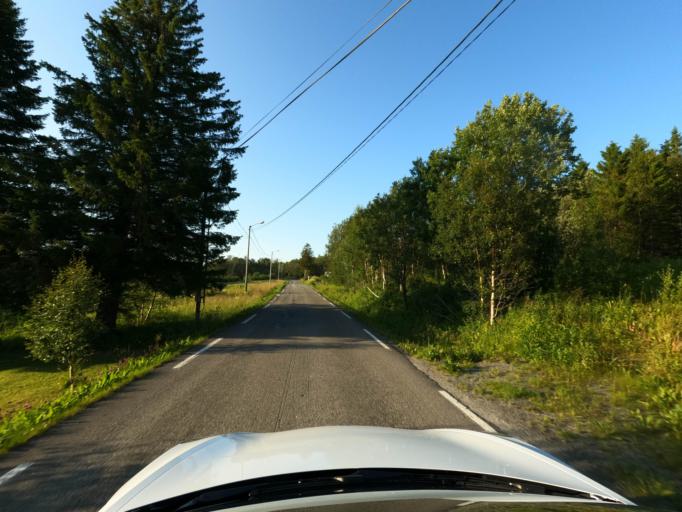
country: NO
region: Nordland
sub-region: Ballangen
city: Ballangen
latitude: 68.4974
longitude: 16.7370
